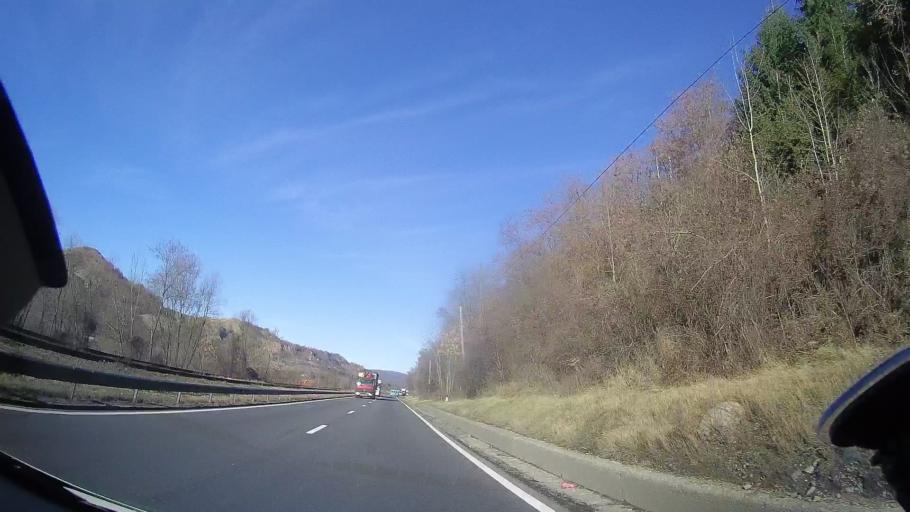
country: RO
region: Cluj
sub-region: Comuna Poeni
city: Poeni
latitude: 46.9017
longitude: 22.8691
